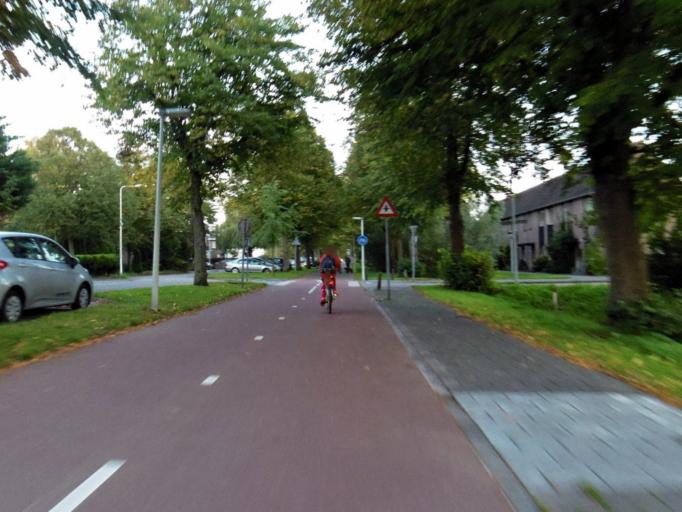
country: NL
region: South Holland
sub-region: Gemeente Oegstgeest
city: Oegstgeest
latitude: 52.1581
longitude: 4.4508
